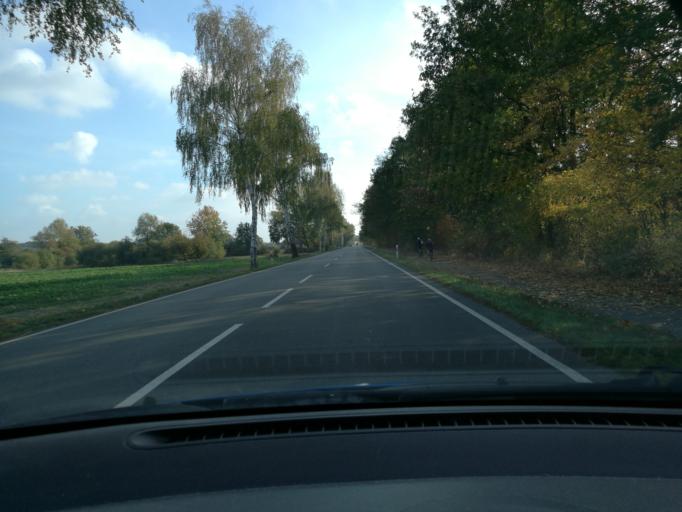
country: DE
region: Lower Saxony
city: Luechow
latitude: 52.9541
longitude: 11.1701
